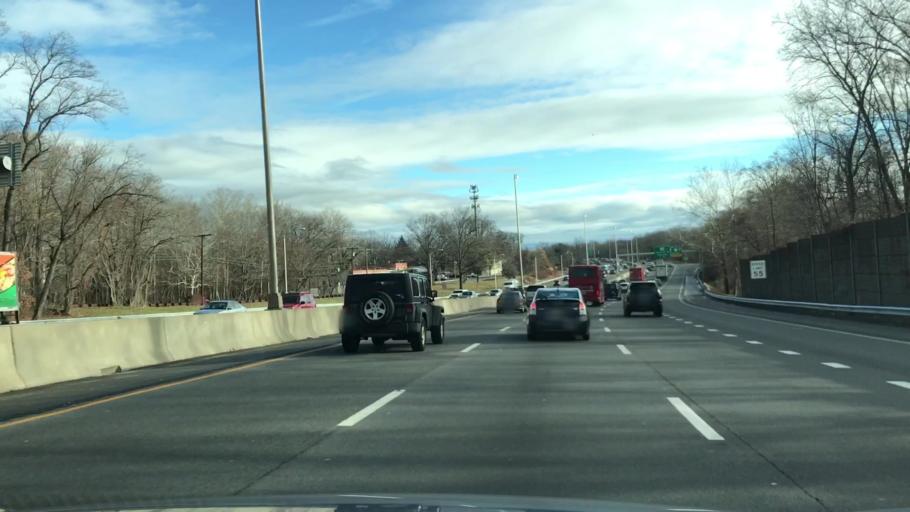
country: US
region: Connecticut
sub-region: Fairfield County
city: Darien
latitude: 41.0705
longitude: -73.4840
